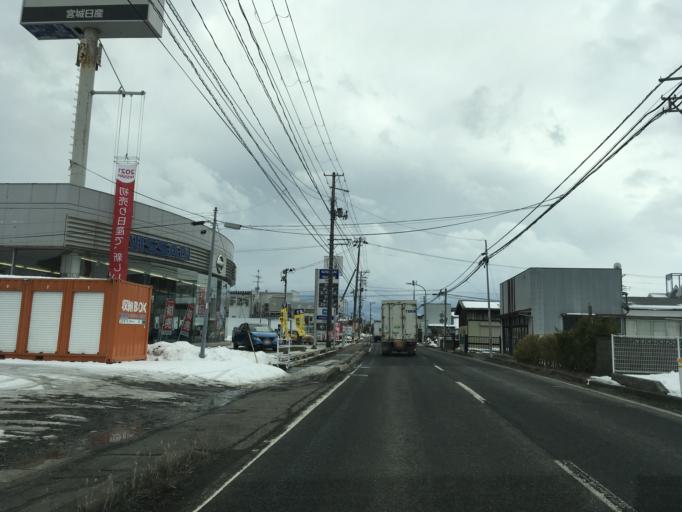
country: JP
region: Miyagi
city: Furukawa
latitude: 38.5849
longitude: 140.9675
